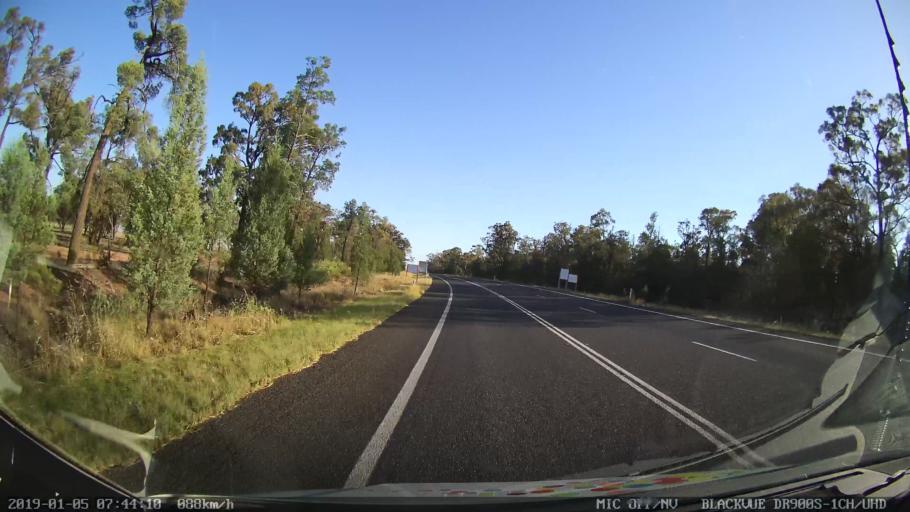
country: AU
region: New South Wales
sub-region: Gilgandra
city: Gilgandra
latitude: -31.8760
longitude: 148.6387
